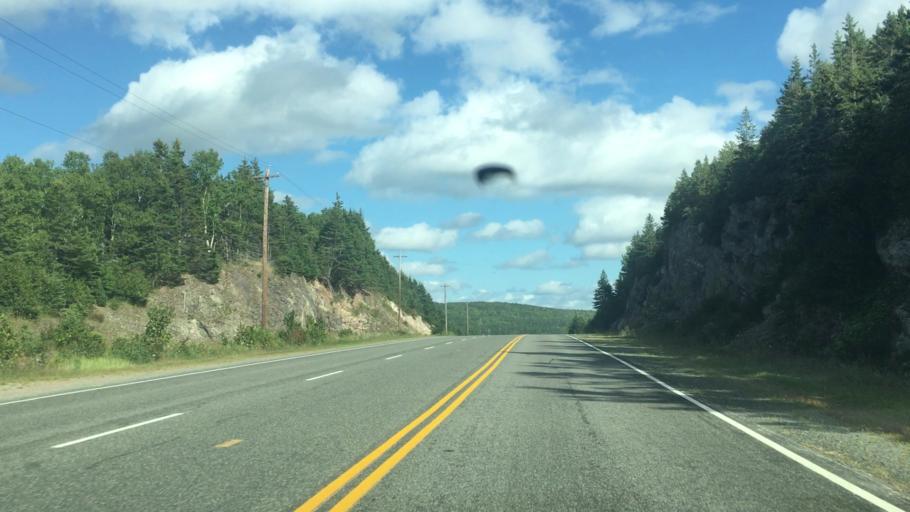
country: CA
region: Nova Scotia
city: Sydney
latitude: 45.8147
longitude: -60.6850
